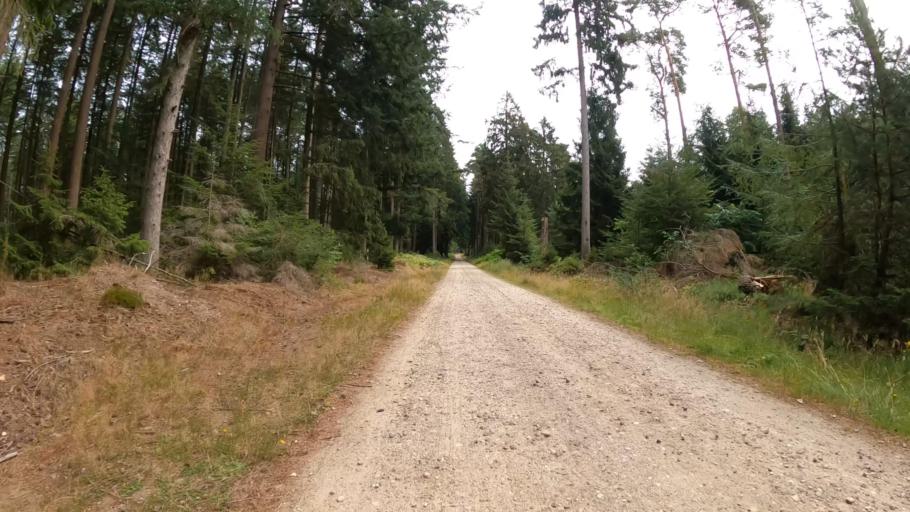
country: DE
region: Schleswig-Holstein
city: Heidmuhlen
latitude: 53.9498
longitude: 10.1237
